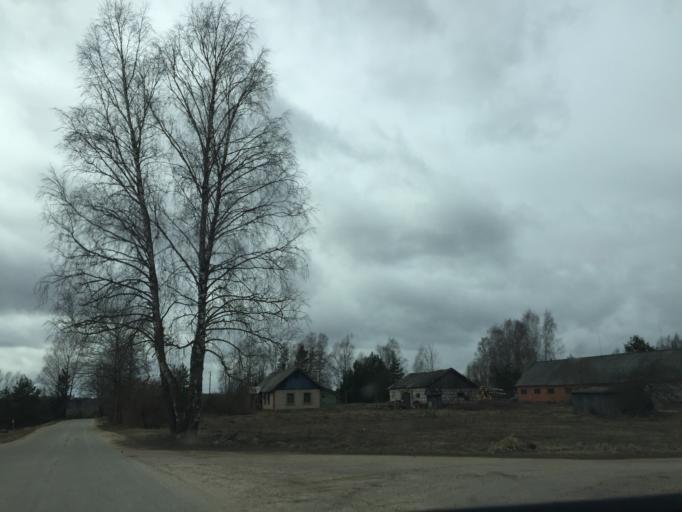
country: LV
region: Kraslavas Rajons
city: Kraslava
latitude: 55.9564
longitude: 27.0331
